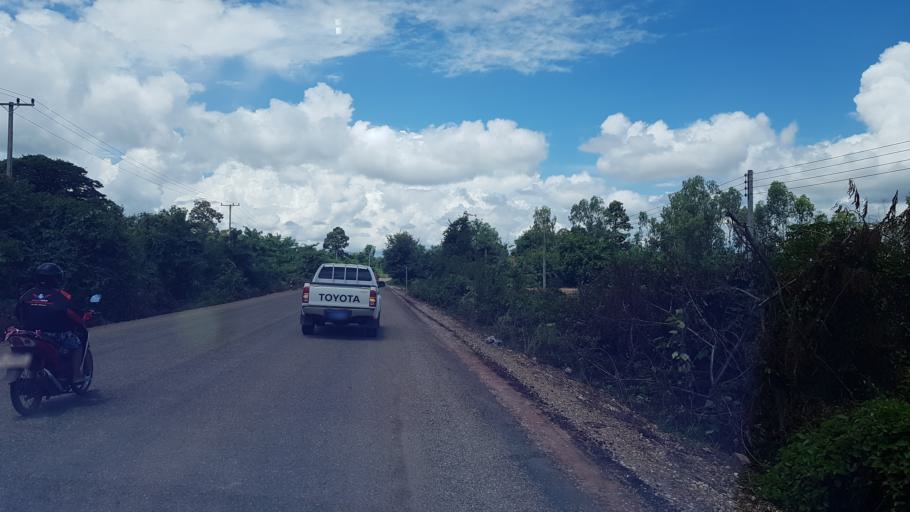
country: LA
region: Vientiane
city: Vientiane
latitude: 18.1120
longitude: 102.5848
